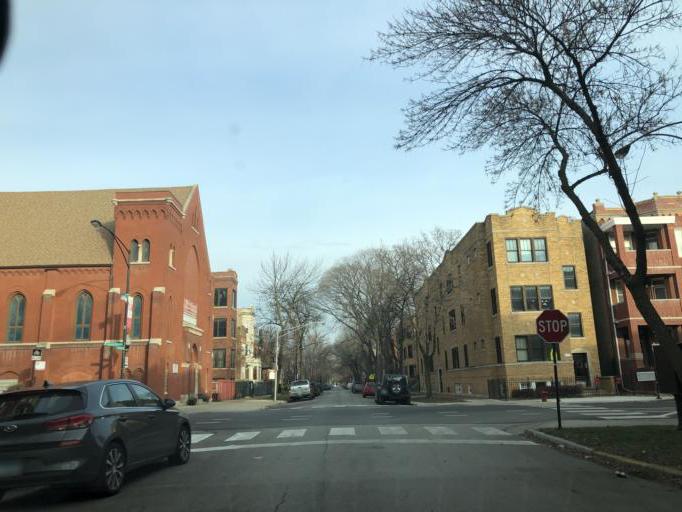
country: US
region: Illinois
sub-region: Cook County
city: Chicago
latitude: 41.8993
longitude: -87.6795
